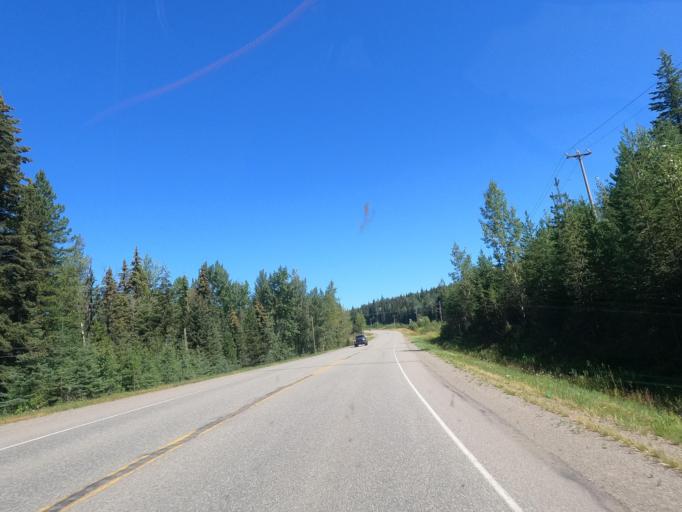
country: CA
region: British Columbia
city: Quesnel
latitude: 53.1396
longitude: -122.3538
